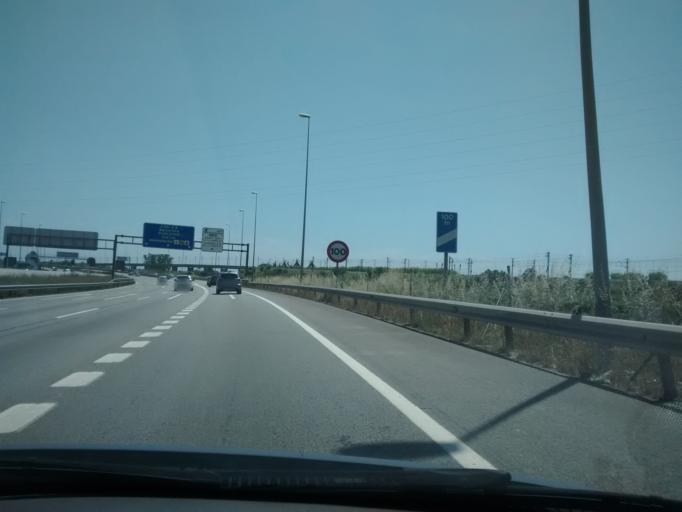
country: ES
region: Catalonia
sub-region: Provincia de Barcelona
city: Sant Joan Despi
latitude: 41.3576
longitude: 2.0513
